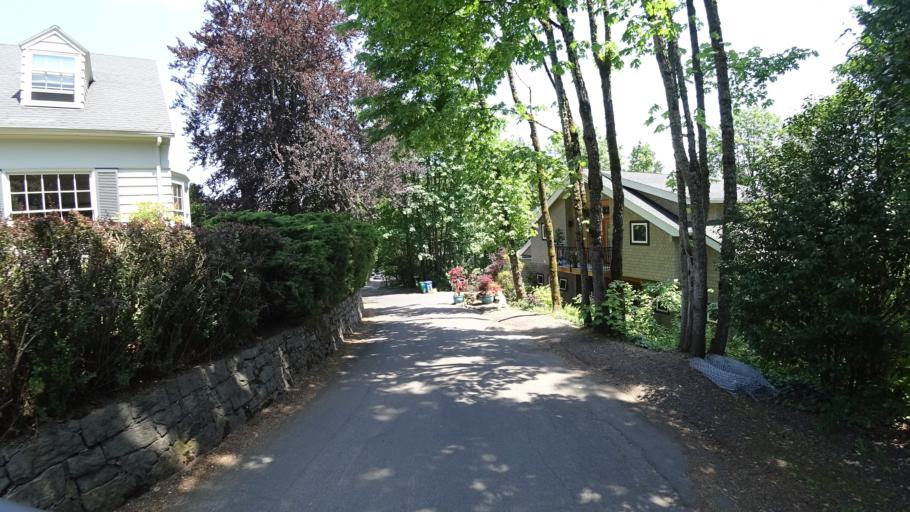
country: US
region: Oregon
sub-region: Multnomah County
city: Portland
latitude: 45.5169
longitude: -122.7120
